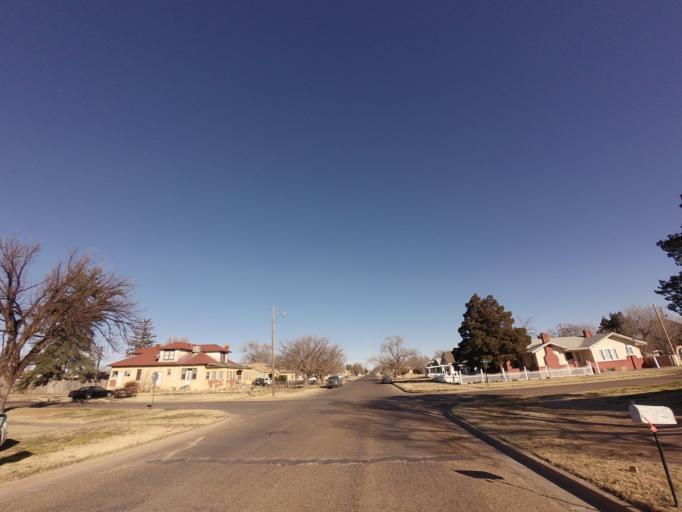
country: US
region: New Mexico
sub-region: Curry County
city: Clovis
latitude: 34.4055
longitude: -103.2079
